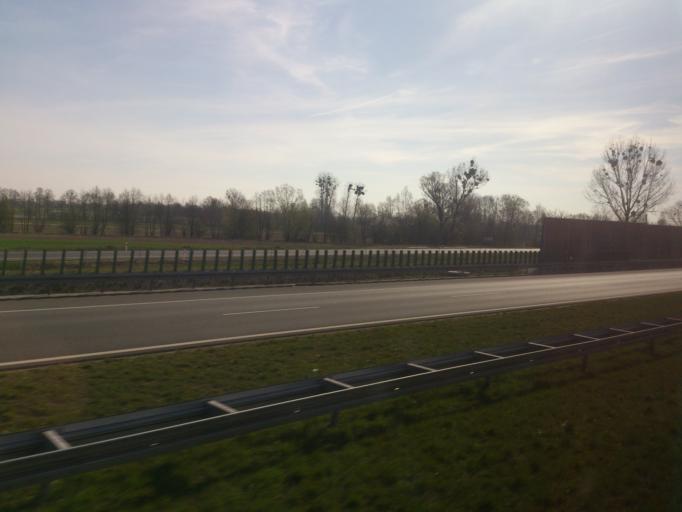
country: PL
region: Kujawsko-Pomorskie
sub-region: Powiat aleksandrowski
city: Waganiec
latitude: 52.7984
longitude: 18.8291
